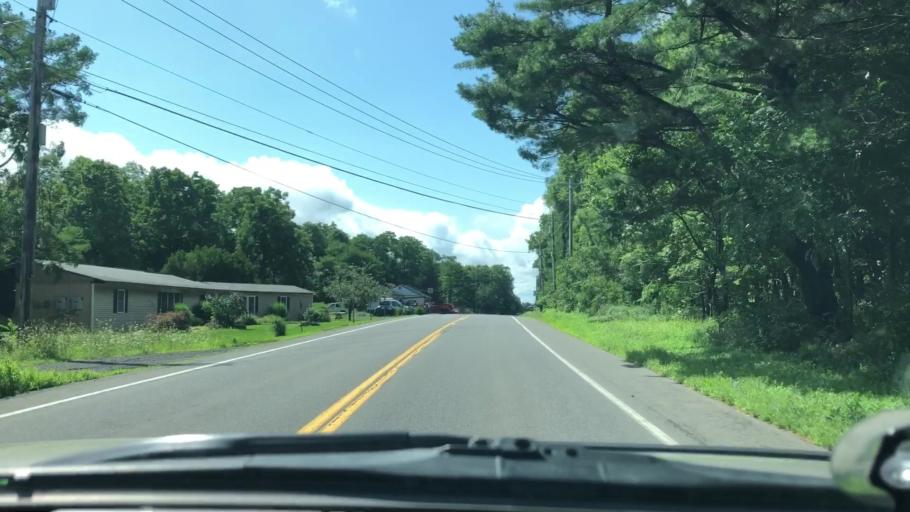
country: US
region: New York
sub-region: Greene County
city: Cairo
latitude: 42.2523
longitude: -73.9783
